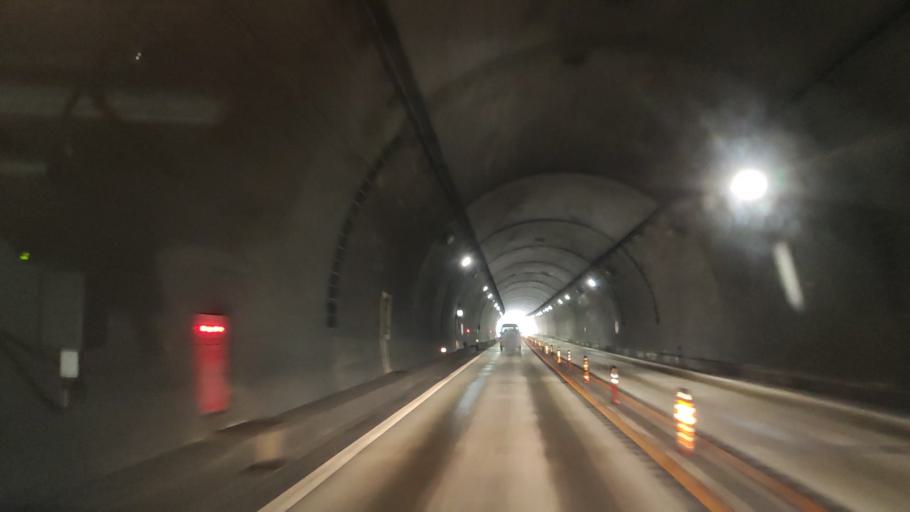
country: JP
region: Tokushima
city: Kamojimacho-jogejima
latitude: 34.1068
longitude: 134.2914
